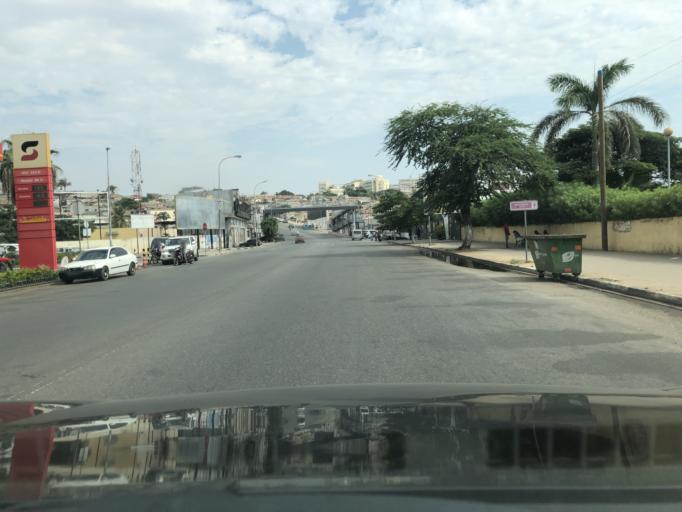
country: AO
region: Luanda
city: Luanda
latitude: -8.8283
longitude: 13.2264
